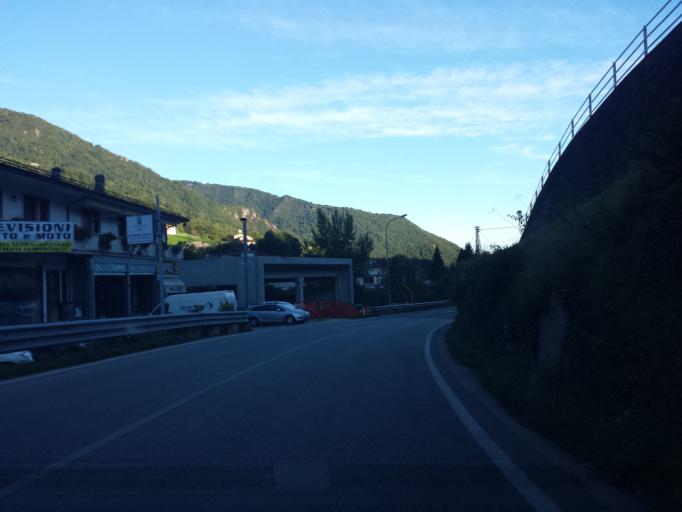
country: IT
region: Veneto
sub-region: Provincia di Vicenza
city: Recoaro Terme
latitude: 45.7006
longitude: 11.2483
